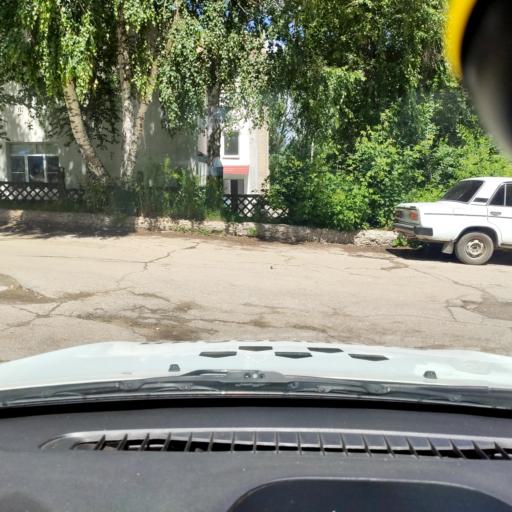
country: RU
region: Samara
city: Zhigulevsk
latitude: 53.4083
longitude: 49.4077
